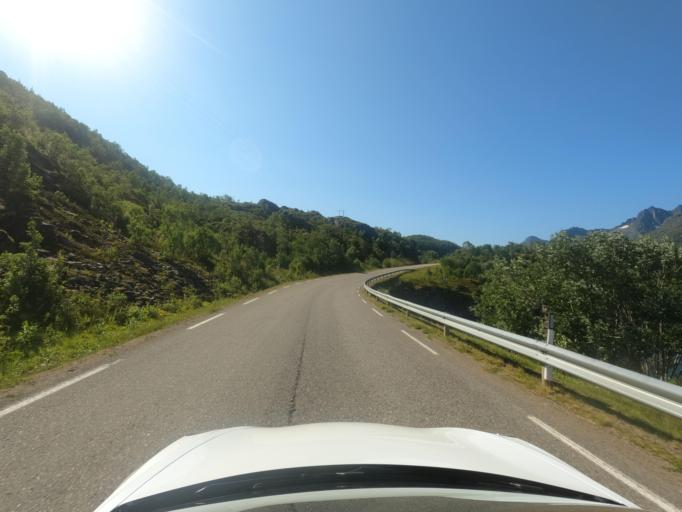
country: NO
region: Nordland
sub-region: Hadsel
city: Stokmarknes
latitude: 68.4386
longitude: 15.1854
